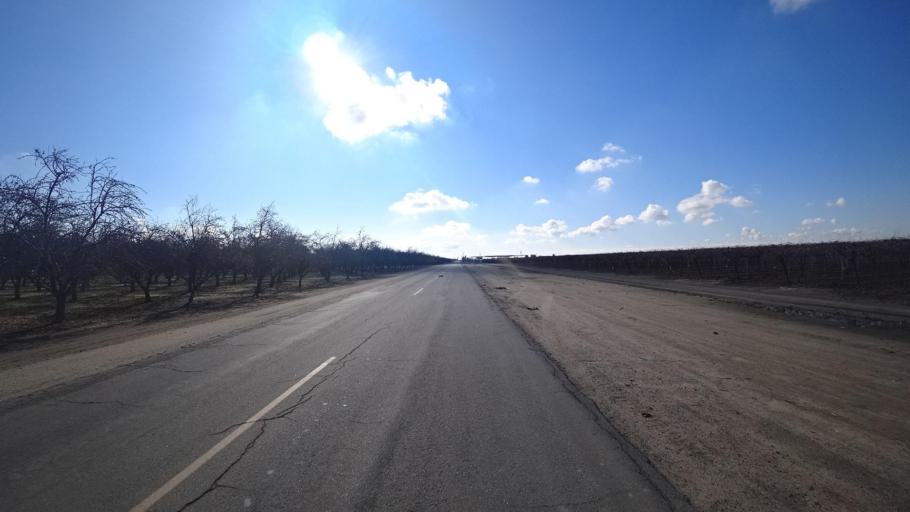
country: US
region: California
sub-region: Kern County
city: McFarland
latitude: 35.7142
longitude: -119.2586
